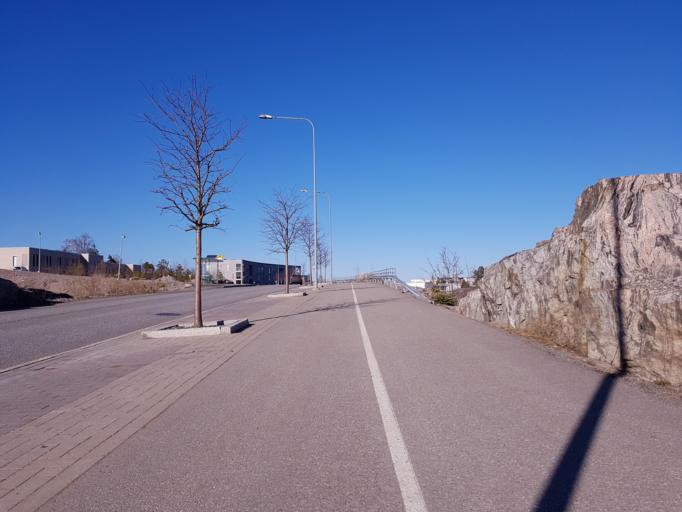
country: FI
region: Uusimaa
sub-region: Helsinki
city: Helsinki
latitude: 60.2274
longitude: 24.9892
